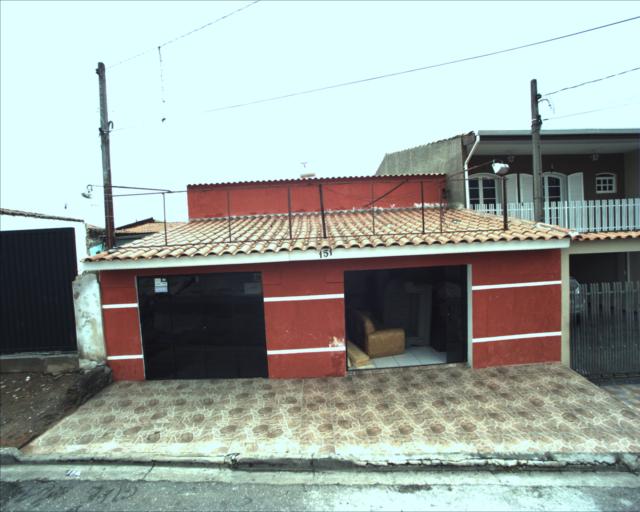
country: BR
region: Sao Paulo
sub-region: Sorocaba
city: Sorocaba
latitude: -23.4576
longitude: -47.4789
